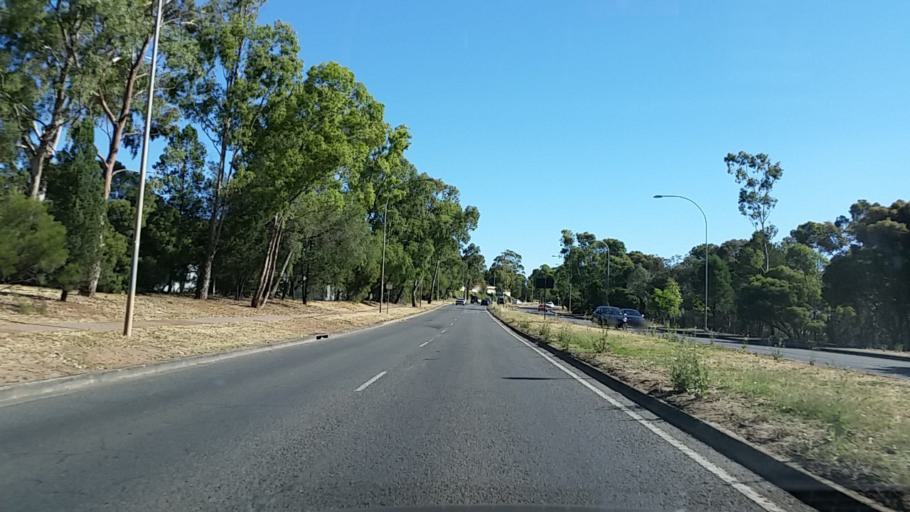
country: AU
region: South Australia
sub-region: Salisbury
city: Ingle Farm
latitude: -34.8166
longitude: 138.6414
